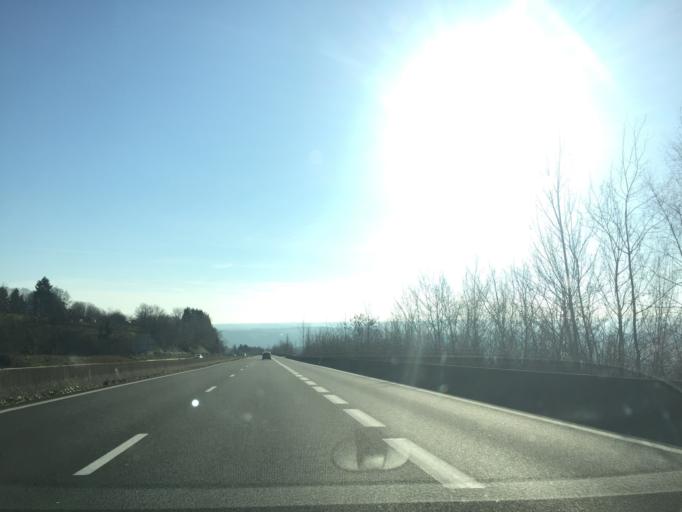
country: FR
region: Limousin
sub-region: Departement de la Correze
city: Donzenac
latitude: 45.2409
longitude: 1.5126
